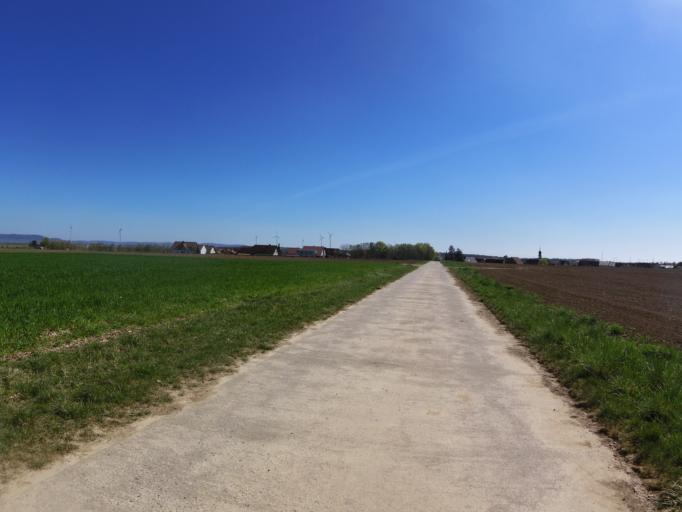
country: DE
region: Bavaria
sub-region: Regierungsbezirk Unterfranken
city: Biebelried
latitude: 49.8010
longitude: 10.0866
